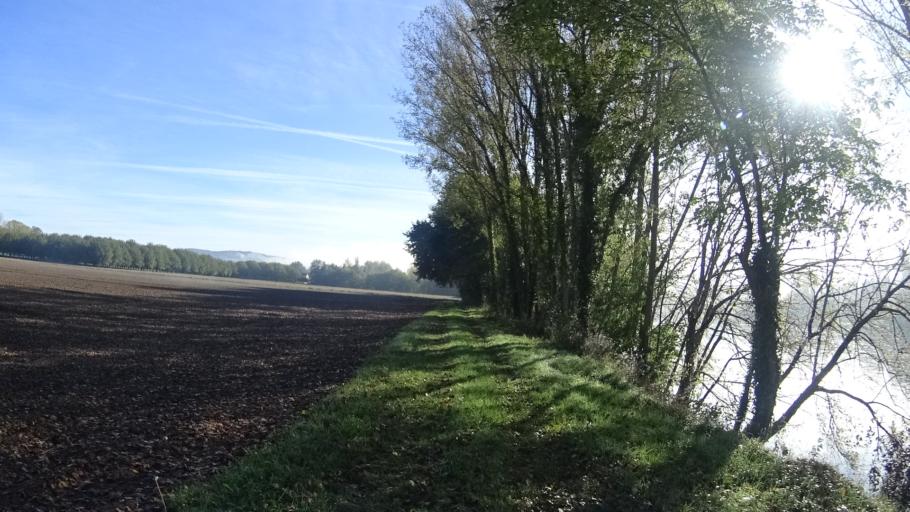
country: FR
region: Aquitaine
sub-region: Departement de la Dordogne
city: Belves
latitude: 44.8281
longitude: 0.9848
